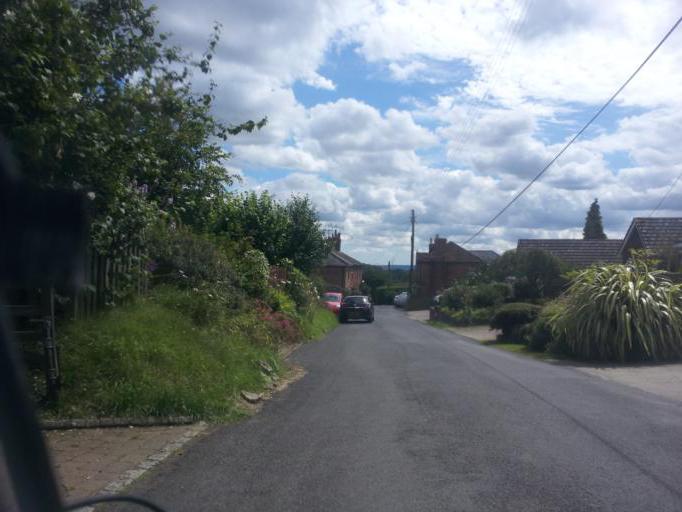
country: GB
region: England
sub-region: Kent
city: Kings Hill
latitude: 51.2658
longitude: 0.3777
